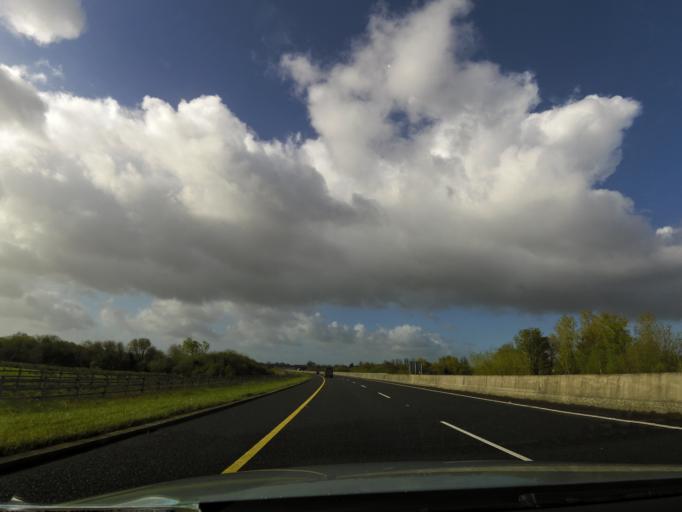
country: IE
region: Munster
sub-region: County Limerick
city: Castleconnell
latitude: 52.6922
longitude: -8.4978
